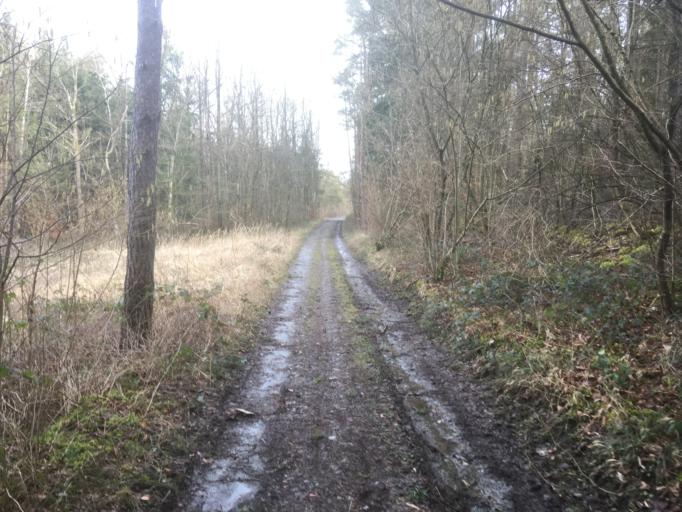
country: BE
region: Wallonia
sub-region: Province du Luxembourg
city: Durbuy
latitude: 50.3179
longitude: 5.4970
